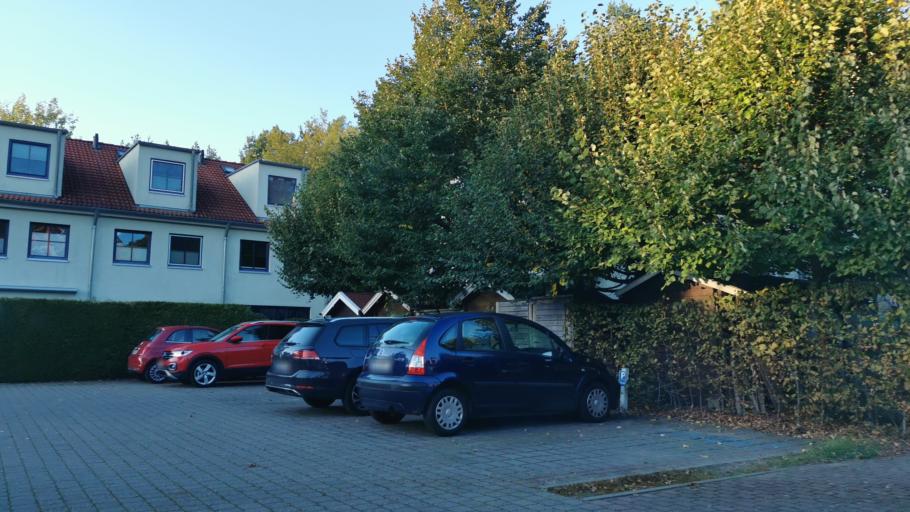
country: DE
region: Brandenburg
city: Michendorf
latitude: 52.3411
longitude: 13.0515
